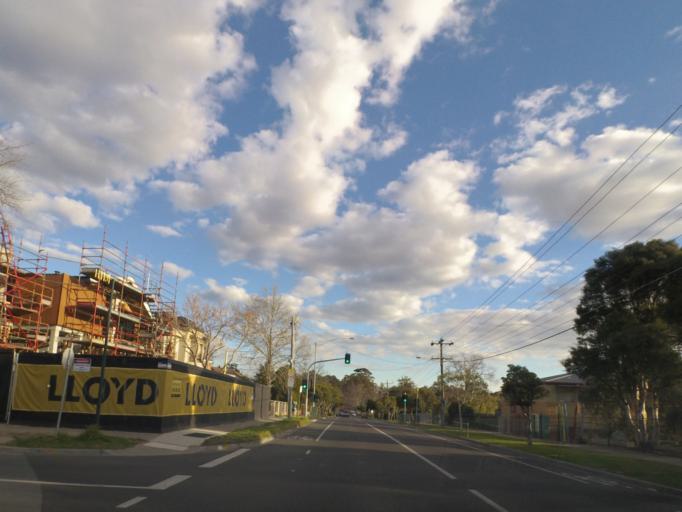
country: AU
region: Victoria
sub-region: Whitehorse
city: Mont Albert North
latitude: -37.8016
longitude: 145.0976
